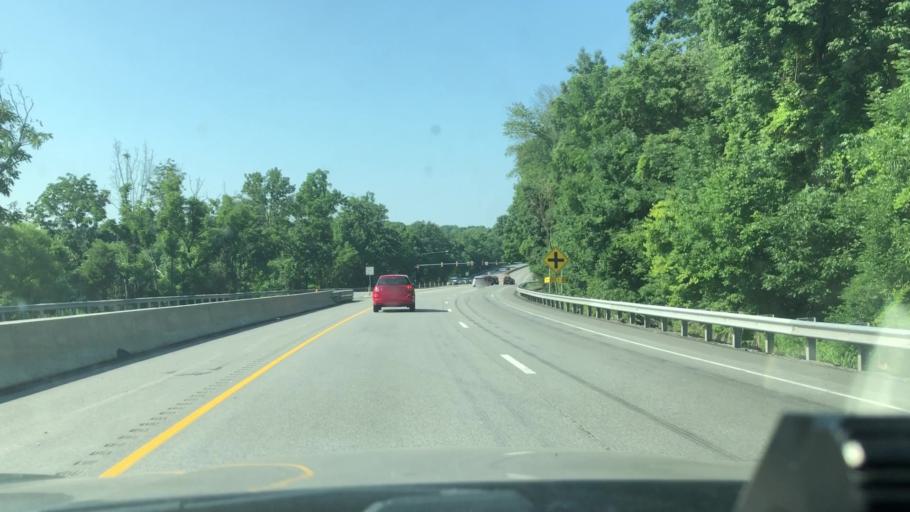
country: US
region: Pennsylvania
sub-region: Montgomery County
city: Halfway House
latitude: 40.2975
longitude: -75.6364
